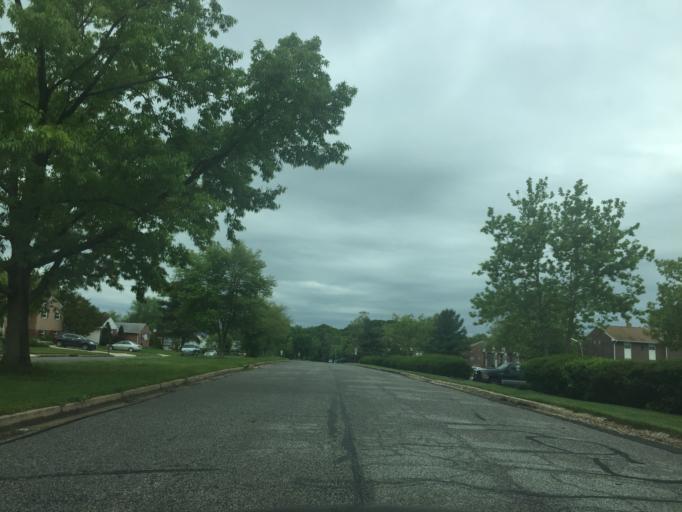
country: US
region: Maryland
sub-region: Baltimore County
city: Perry Hall
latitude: 39.4092
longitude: -76.4619
